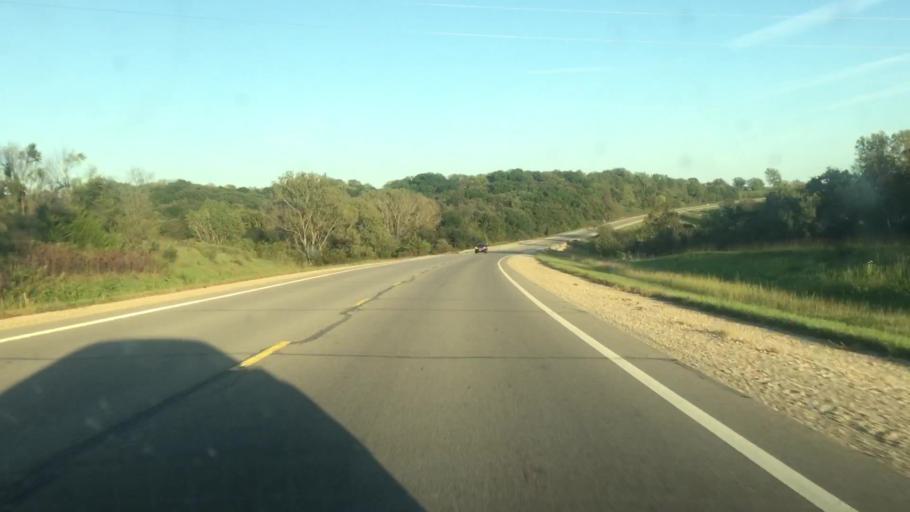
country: US
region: Kansas
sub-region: Atchison County
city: Atchison
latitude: 39.4845
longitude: -95.1169
